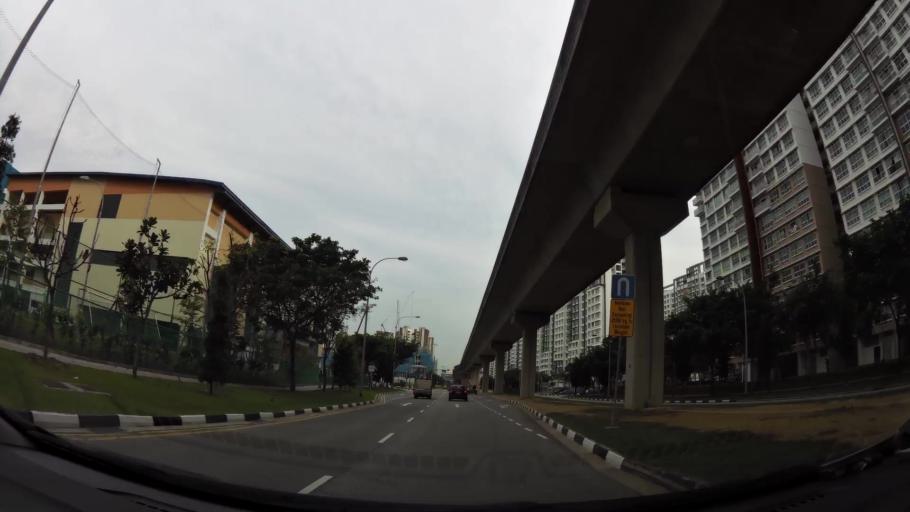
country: MY
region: Johor
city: Kampung Pasir Gudang Baru
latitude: 1.4044
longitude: 103.9100
